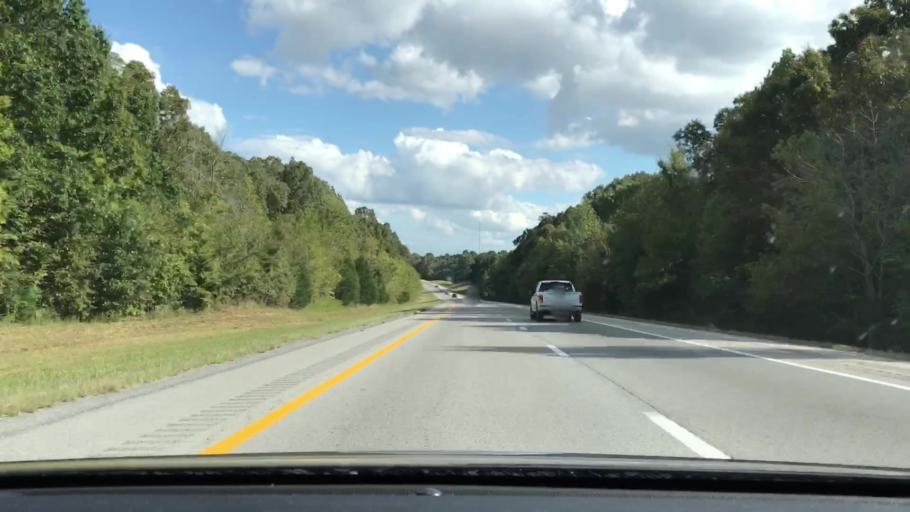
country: US
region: Kentucky
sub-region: Caldwell County
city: Princeton
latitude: 37.0053
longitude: -87.9692
